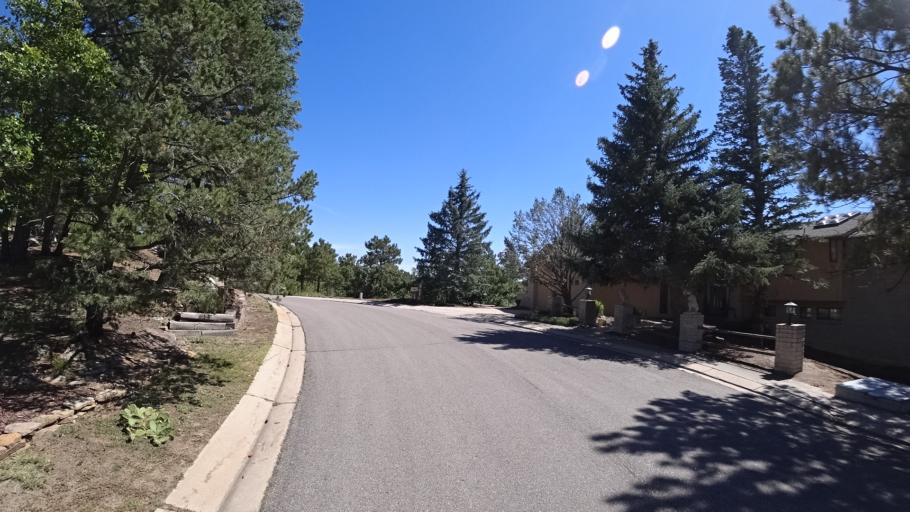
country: US
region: Colorado
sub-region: El Paso County
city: Colorado Springs
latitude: 38.9187
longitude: -104.7976
